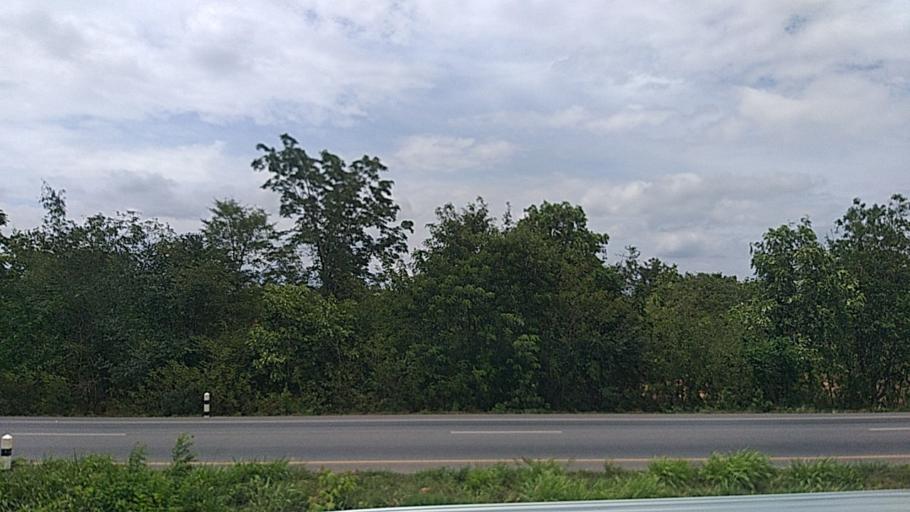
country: TH
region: Nakhon Ratchasima
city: Sung Noen
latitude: 14.8284
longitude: 101.8015
